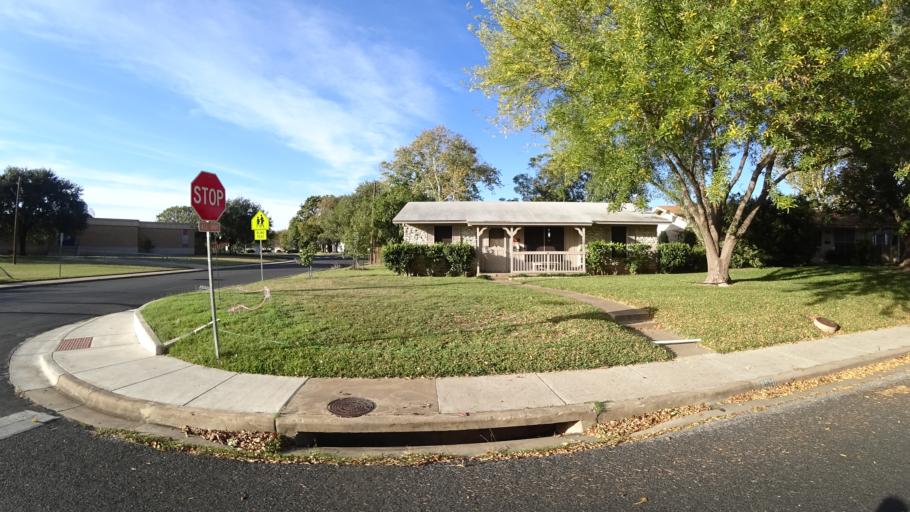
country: US
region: Texas
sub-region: Williamson County
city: Jollyville
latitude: 30.3687
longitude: -97.7320
